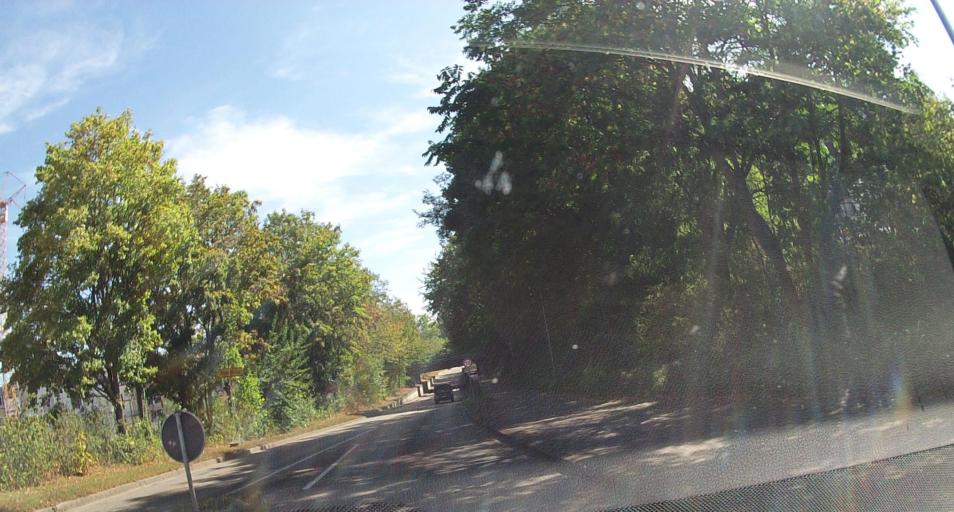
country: DE
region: Baden-Wuerttemberg
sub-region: Karlsruhe Region
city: Rastatt
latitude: 48.8494
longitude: 8.2127
